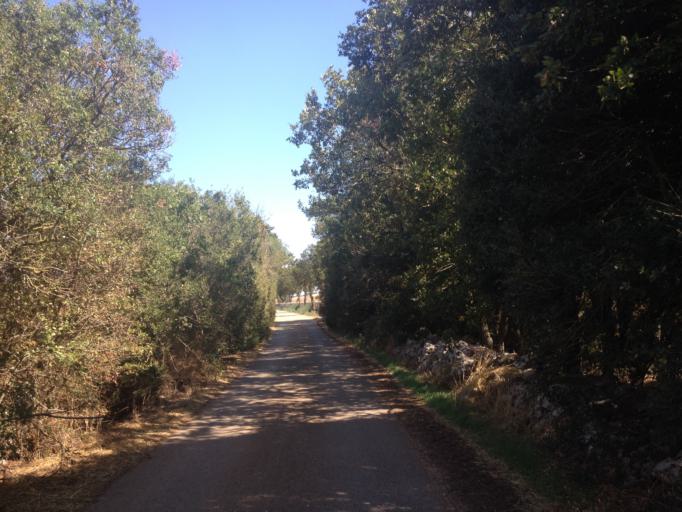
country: IT
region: Apulia
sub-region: Provincia di Bari
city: Sammichele di Bari
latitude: 40.8226
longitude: 17.0140
